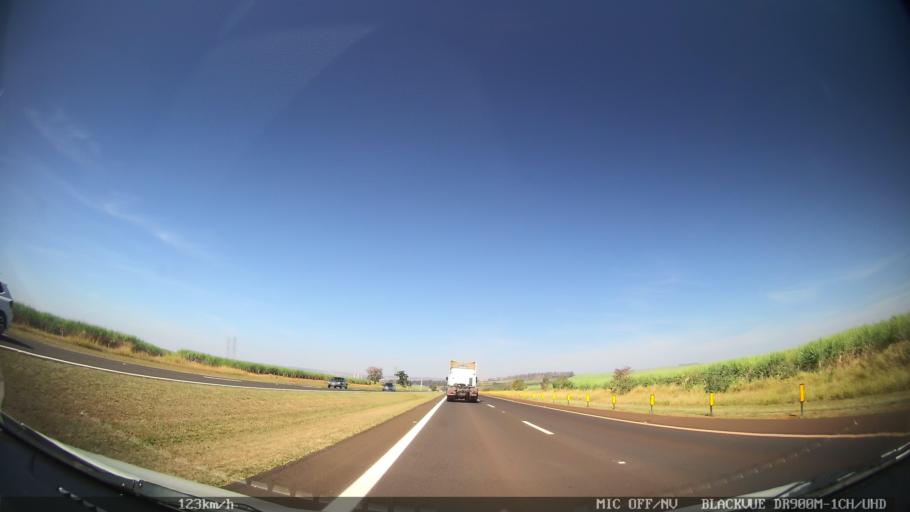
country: BR
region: Sao Paulo
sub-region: Ribeirao Preto
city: Ribeirao Preto
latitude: -21.1831
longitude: -47.8908
